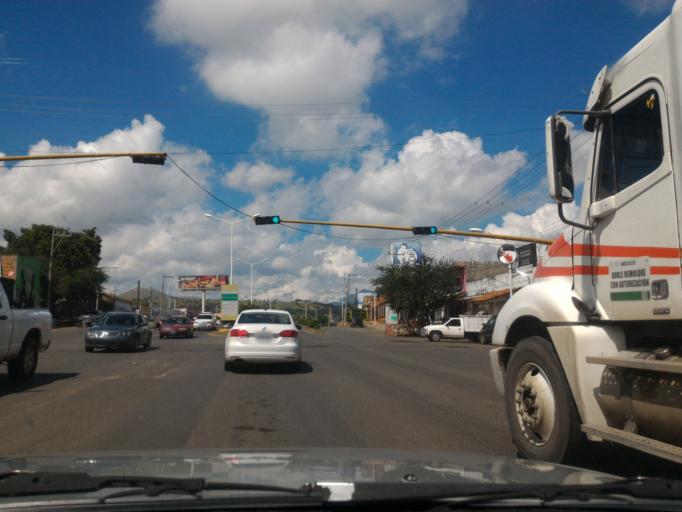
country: MX
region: Jalisco
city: Tequila
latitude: 20.8805
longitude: -103.8288
